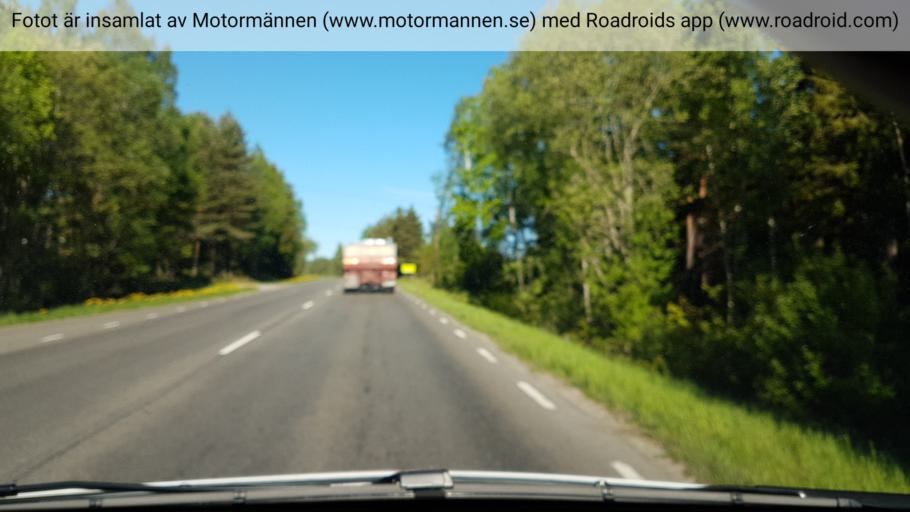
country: SE
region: Vaestra Goetaland
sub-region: Skovde Kommun
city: Stopen
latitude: 58.5271
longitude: 13.8005
